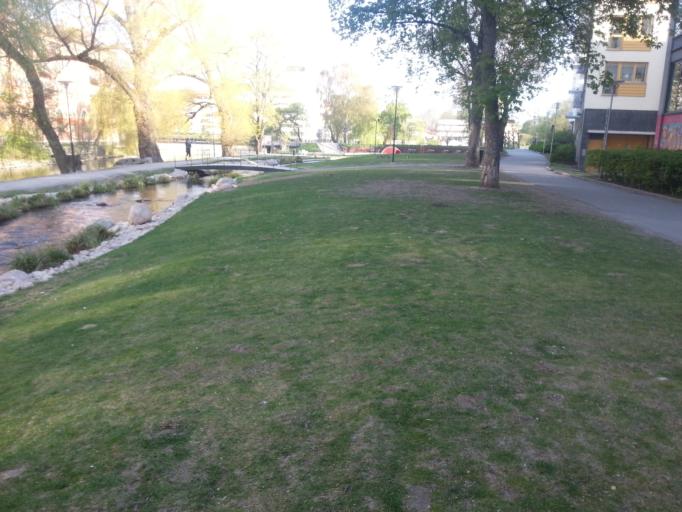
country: SE
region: OEstergoetland
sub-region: Norrkopings Kommun
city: Norrkoping
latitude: 58.5909
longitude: 16.1845
